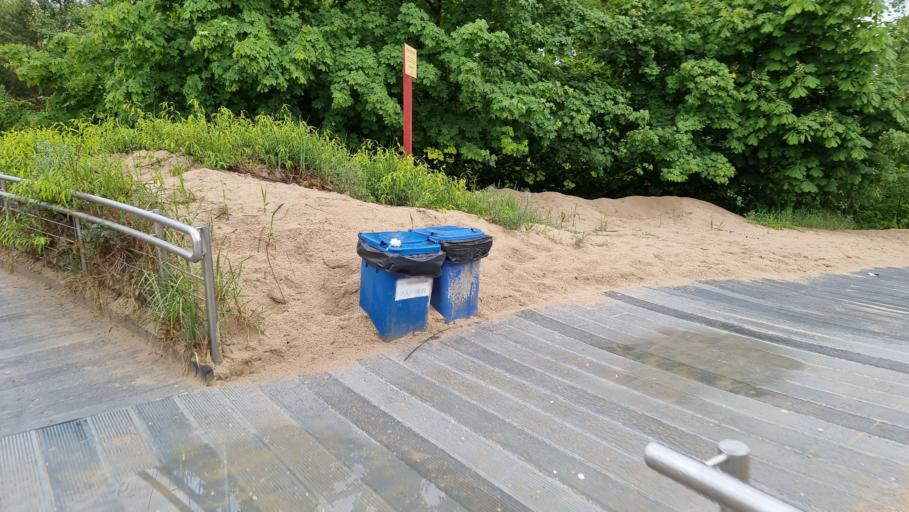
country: PL
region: West Pomeranian Voivodeship
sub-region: Swinoujscie
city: Swinoujscie
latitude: 53.9219
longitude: 14.2499
